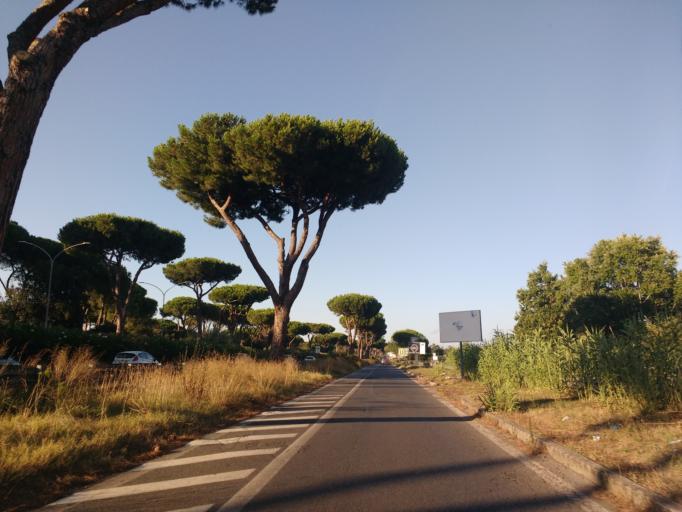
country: IT
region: Latium
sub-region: Citta metropolitana di Roma Capitale
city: Acilia-Castel Fusano-Ostia Antica
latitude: 41.7495
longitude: 12.3630
